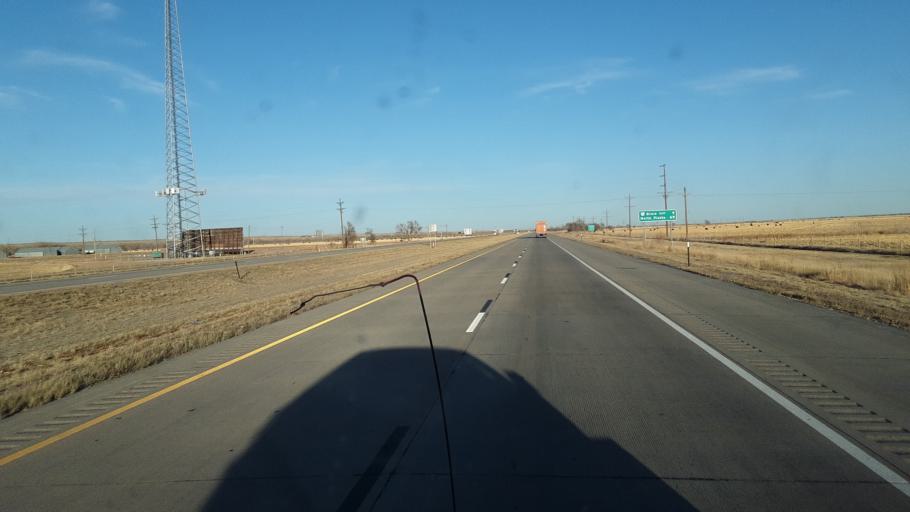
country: US
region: Colorado
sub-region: Sedgwick County
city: Julesburg
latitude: 41.0526
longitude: -102.0579
